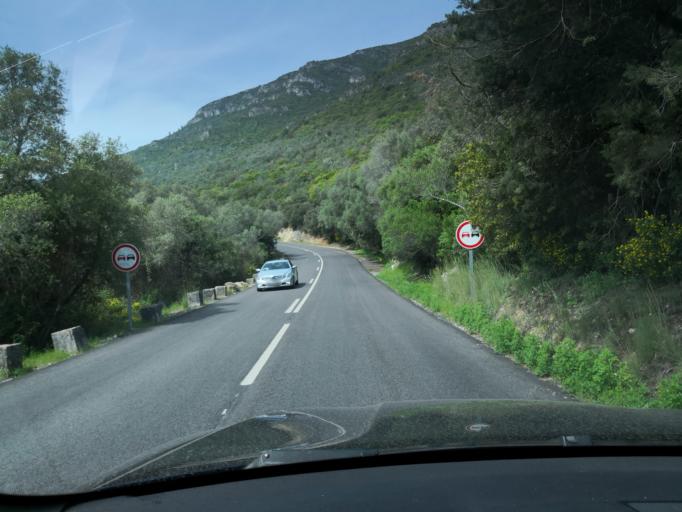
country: PT
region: Setubal
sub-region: Palmela
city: Quinta do Anjo
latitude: 38.4841
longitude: -8.9769
